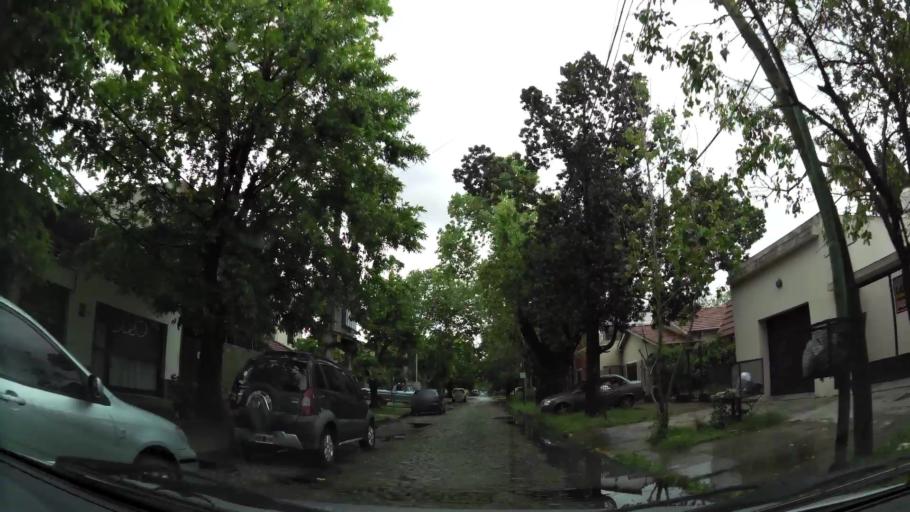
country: AR
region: Buenos Aires
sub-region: Partido de Lomas de Zamora
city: Lomas de Zamora
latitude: -34.7516
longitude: -58.3917
